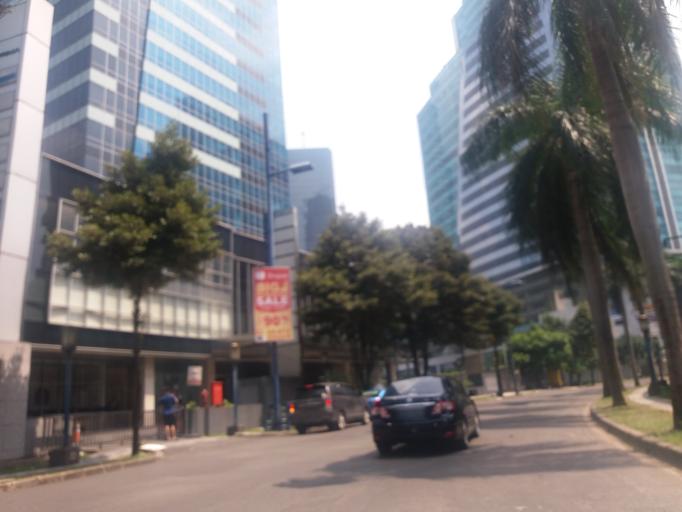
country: ID
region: Jakarta Raya
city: Jakarta
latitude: -6.2299
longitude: 106.8263
